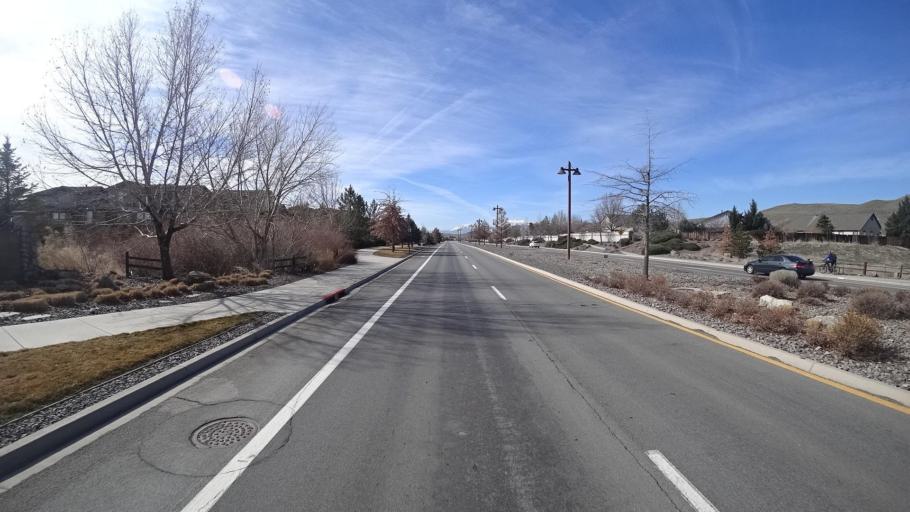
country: US
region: Nevada
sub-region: Washoe County
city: Sun Valley
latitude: 39.5994
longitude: -119.7292
